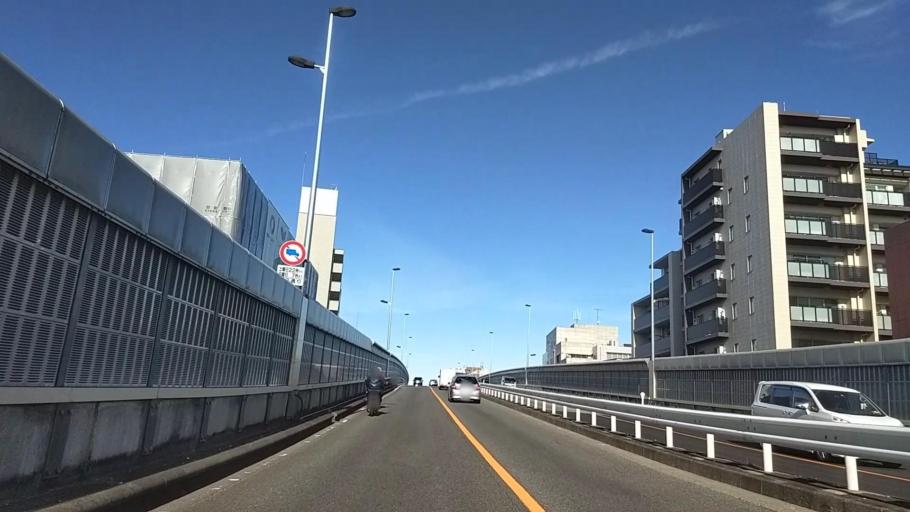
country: JP
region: Kanagawa
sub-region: Kawasaki-shi
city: Kawasaki
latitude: 35.5875
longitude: 139.6787
